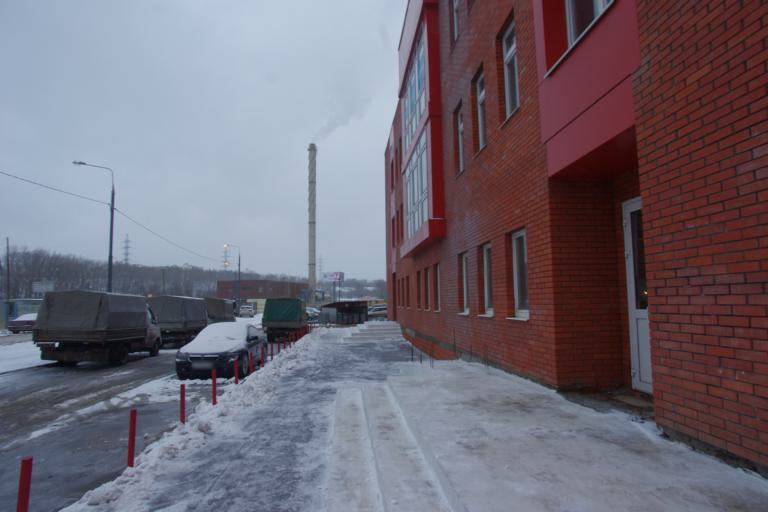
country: RU
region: Moskovskaya
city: Pavshino
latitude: 55.8223
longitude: 37.3639
